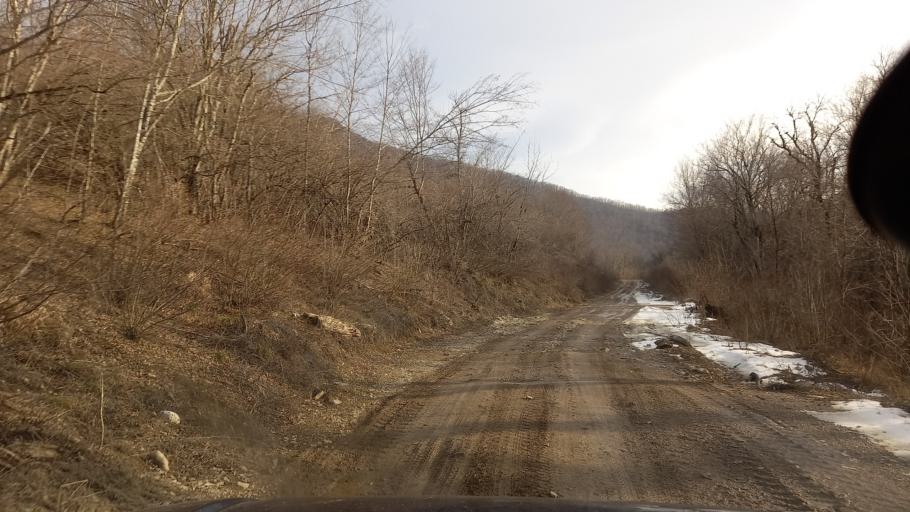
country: RU
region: Adygeya
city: Kamennomostskiy
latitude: 44.1510
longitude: 40.2962
